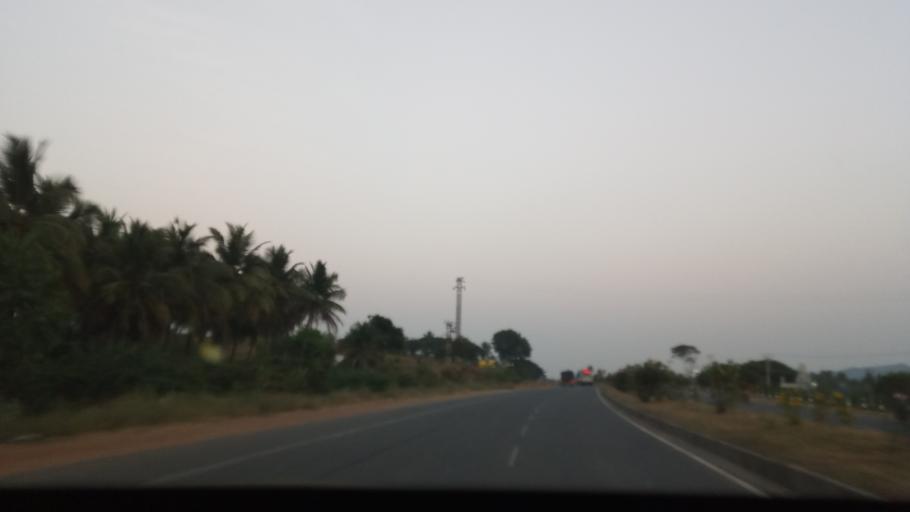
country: IN
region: Tamil Nadu
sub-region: Salem
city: Belur
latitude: 11.6523
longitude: 78.3538
